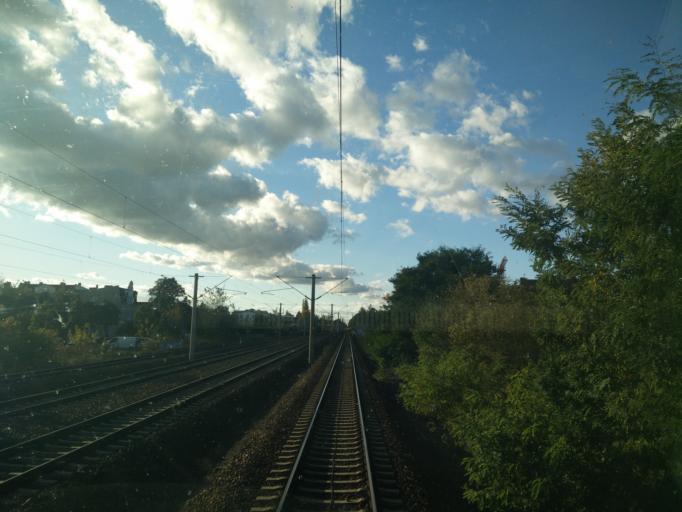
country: DE
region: Brandenburg
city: Falkensee
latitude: 52.5590
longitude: 13.0927
